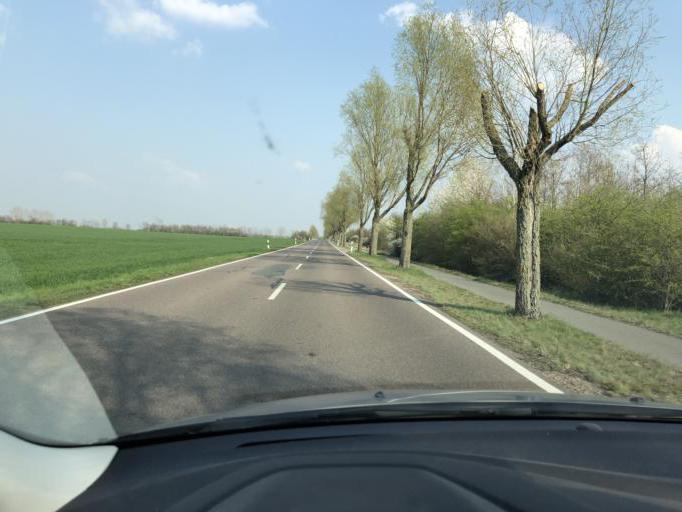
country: DE
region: Saxony
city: Zwochau
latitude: 51.4360
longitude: 12.2519
